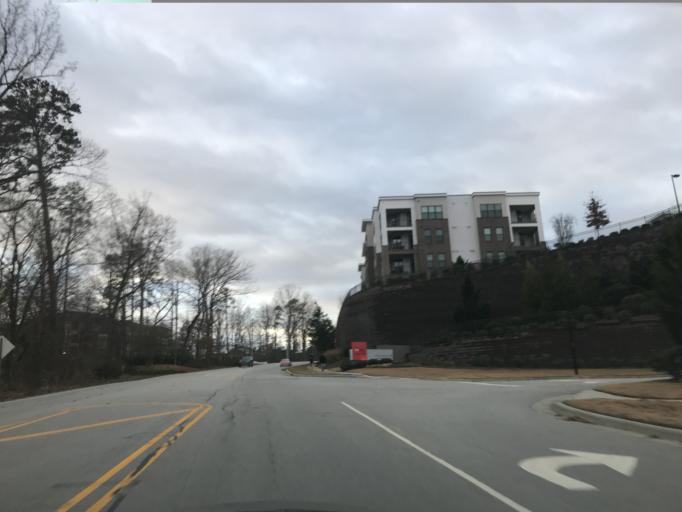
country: US
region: North Carolina
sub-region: Wake County
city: West Raleigh
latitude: 35.8342
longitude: -78.6779
